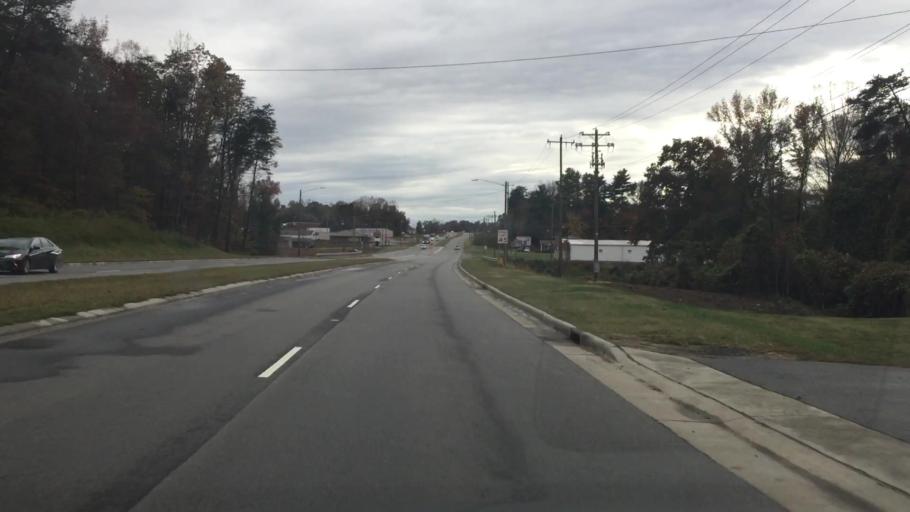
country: US
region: North Carolina
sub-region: Rockingham County
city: Reidsville
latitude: 36.3638
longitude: -79.6830
